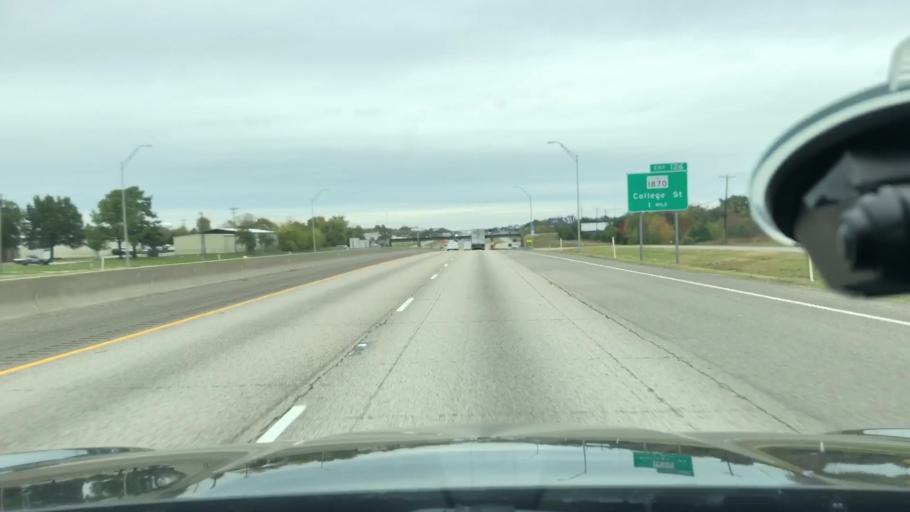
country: US
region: Texas
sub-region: Hopkins County
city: Sulphur Springs
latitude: 33.1235
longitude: -95.5827
